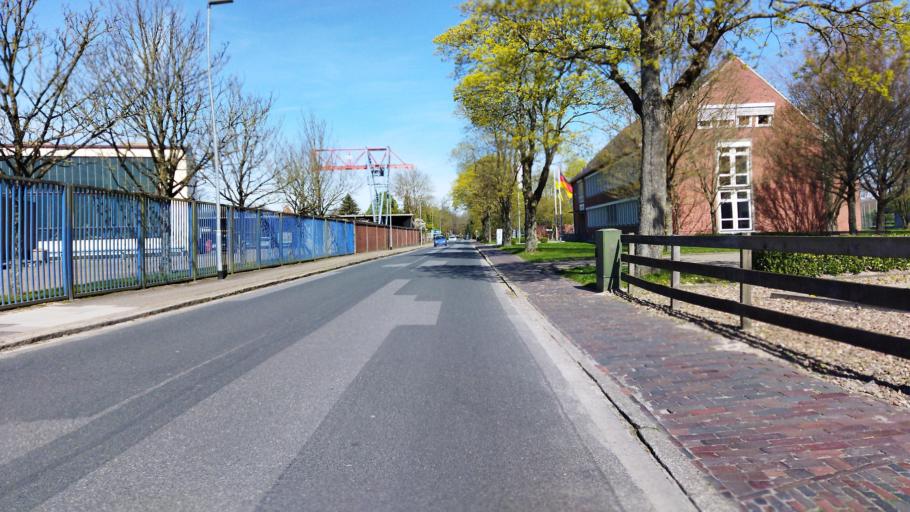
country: DE
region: Lower Saxony
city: Brake (Unterweser)
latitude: 53.3323
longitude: 8.4854
